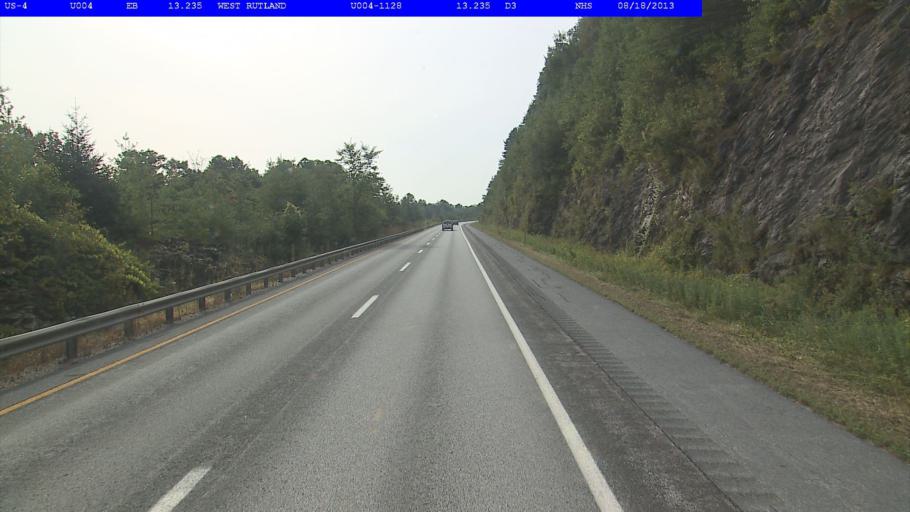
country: US
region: Vermont
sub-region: Rutland County
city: West Rutland
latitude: 43.6027
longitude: -73.0626
